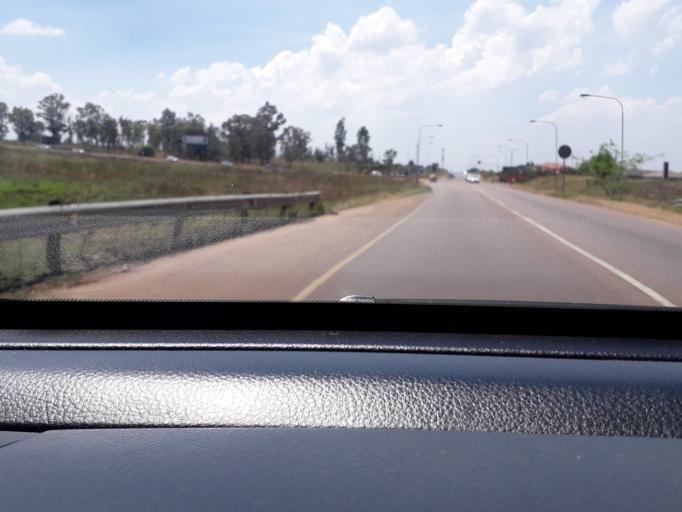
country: ZA
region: Gauteng
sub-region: City of Tshwane Metropolitan Municipality
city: Centurion
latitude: -25.9159
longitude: 28.1838
